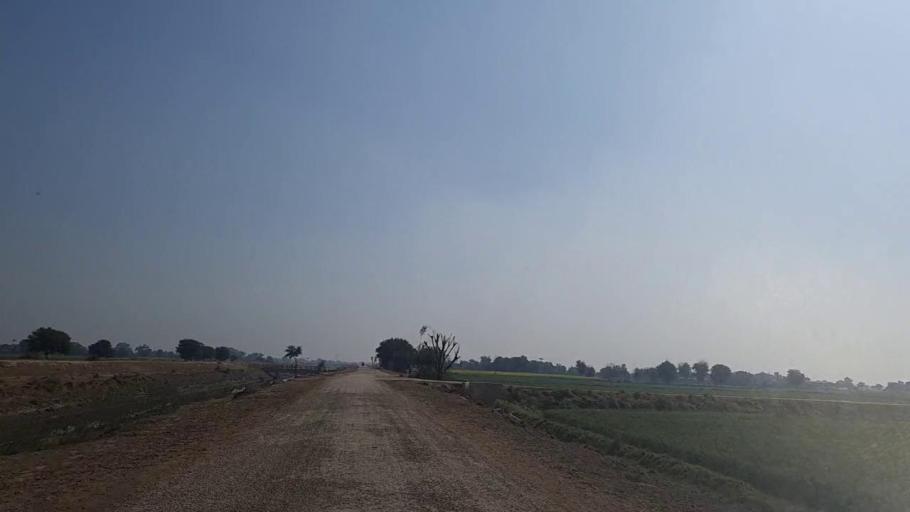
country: PK
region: Sindh
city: Shahpur Chakar
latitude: 26.1822
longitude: 68.5662
